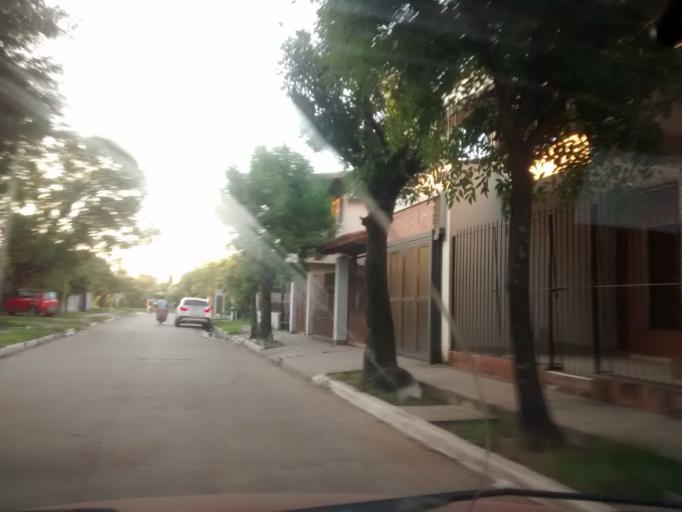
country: AR
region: Chaco
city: Fontana
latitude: -27.4422
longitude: -59.0139
